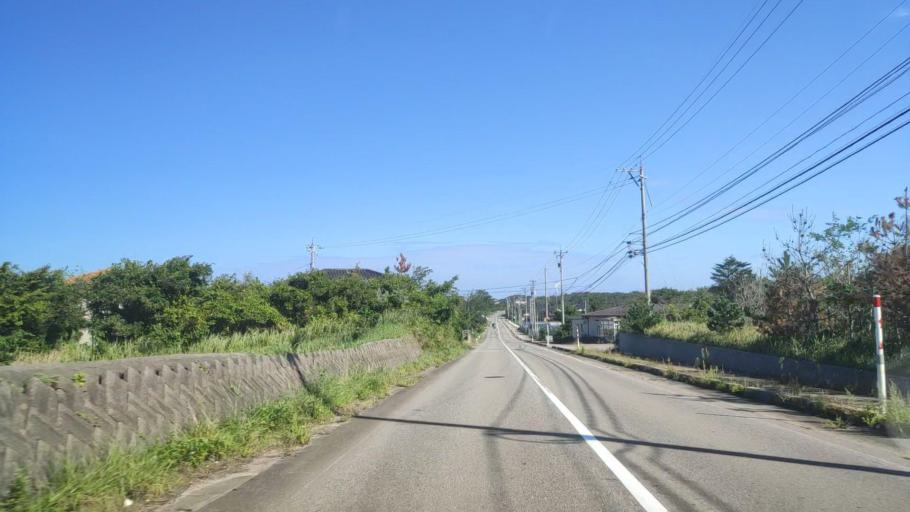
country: JP
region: Ishikawa
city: Hakui
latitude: 36.9802
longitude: 136.7765
